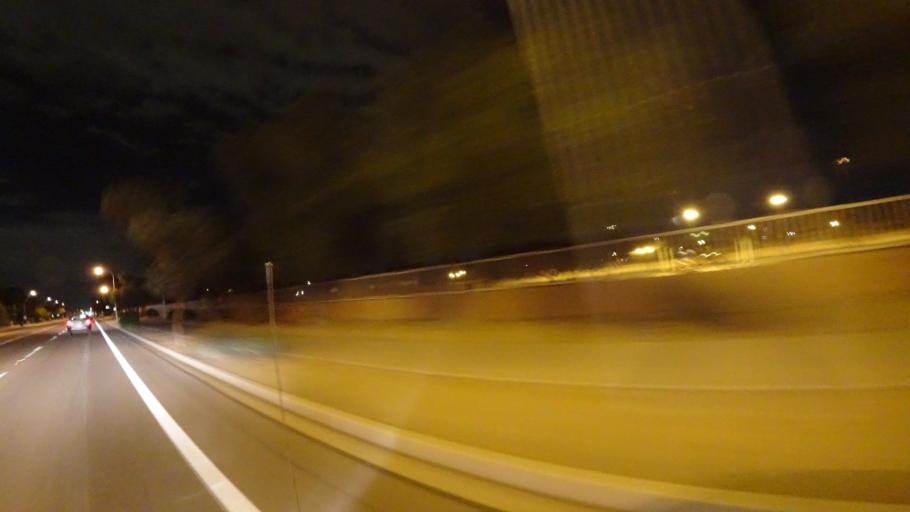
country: US
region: Arizona
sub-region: Maricopa County
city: San Carlos
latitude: 33.3367
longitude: -111.9111
